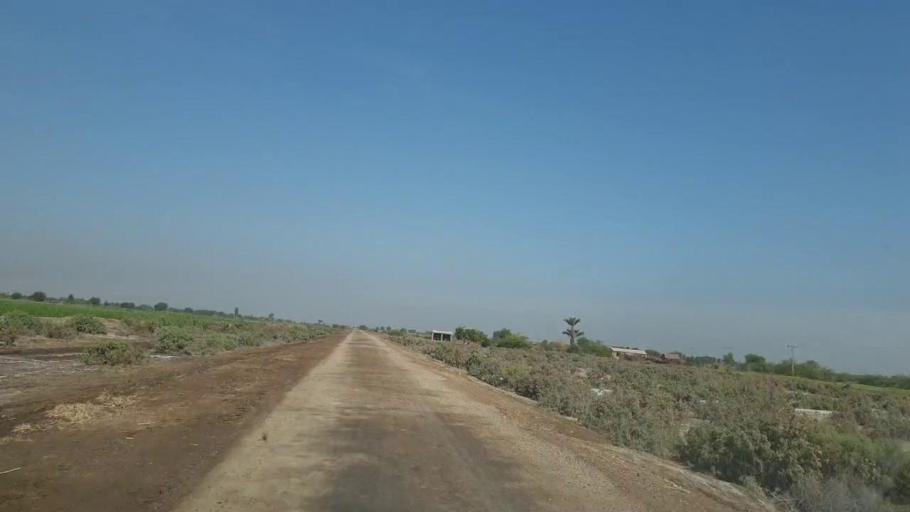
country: PK
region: Sindh
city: Mirpur Khas
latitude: 25.5716
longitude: 69.1846
